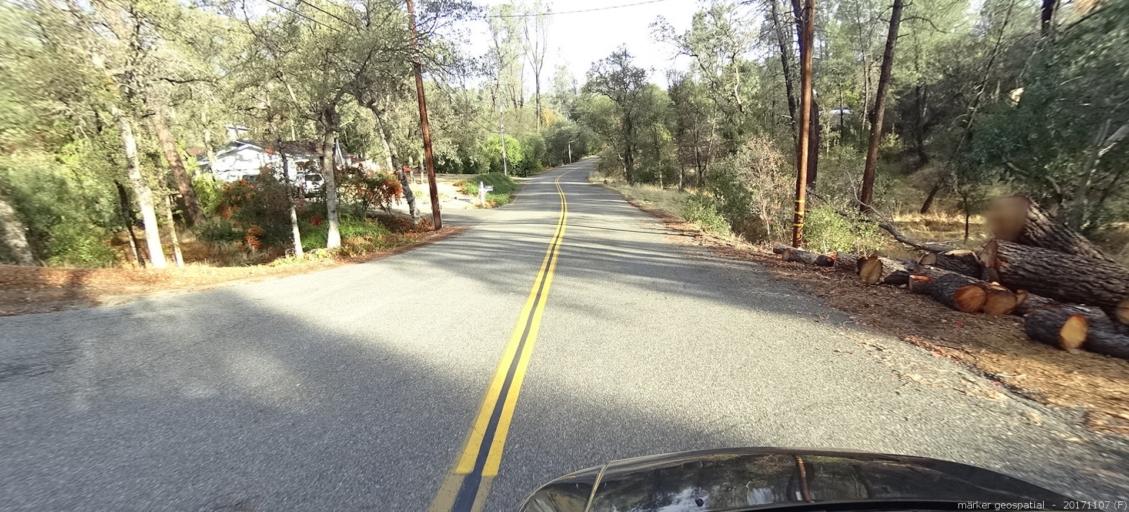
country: US
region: California
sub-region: Shasta County
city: Shasta
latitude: 40.5803
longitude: -122.4672
